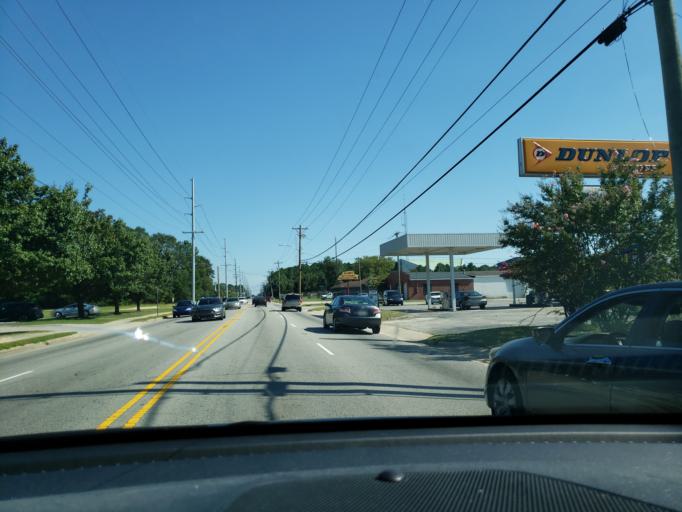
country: US
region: North Carolina
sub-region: Cumberland County
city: Fayetteville
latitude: 35.0919
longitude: -78.9113
